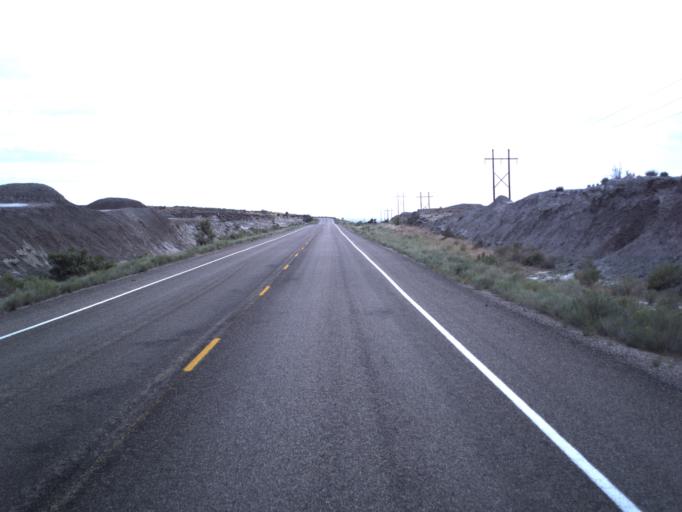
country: US
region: Colorado
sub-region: Rio Blanco County
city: Rangely
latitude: 40.1027
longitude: -109.2264
